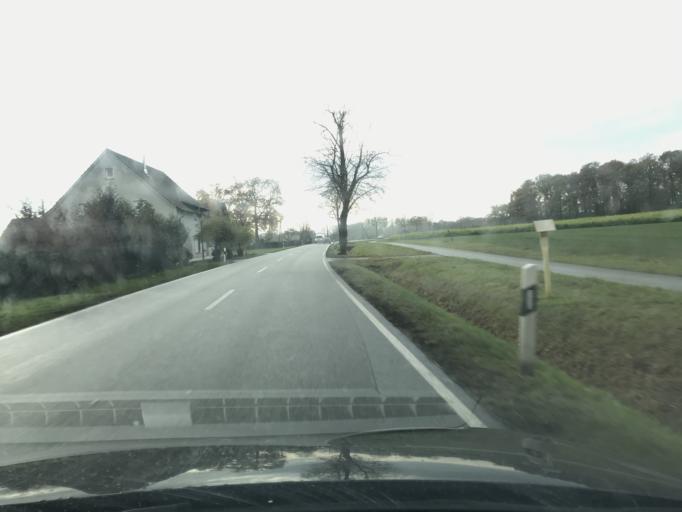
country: DE
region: North Rhine-Westphalia
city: Oelde
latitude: 51.8408
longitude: 8.1804
